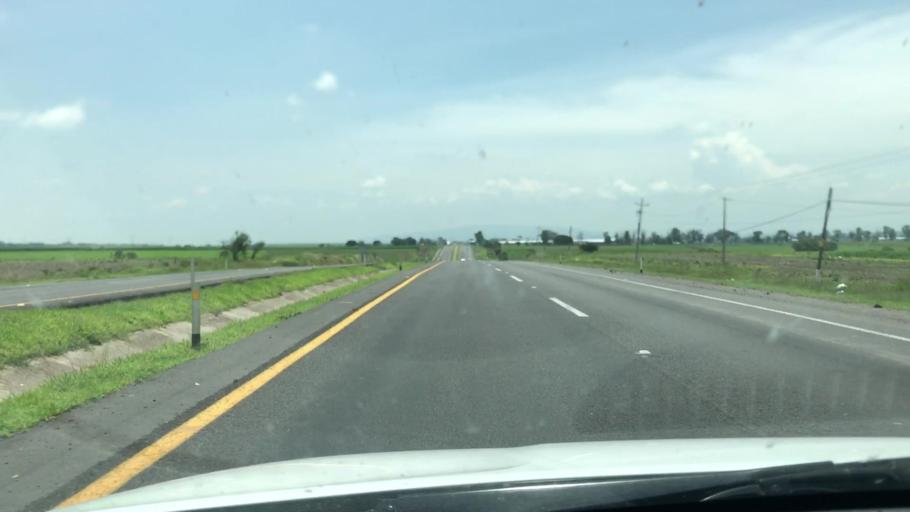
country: MX
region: Guanajuato
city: Penjamo
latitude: 20.3851
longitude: -101.7838
